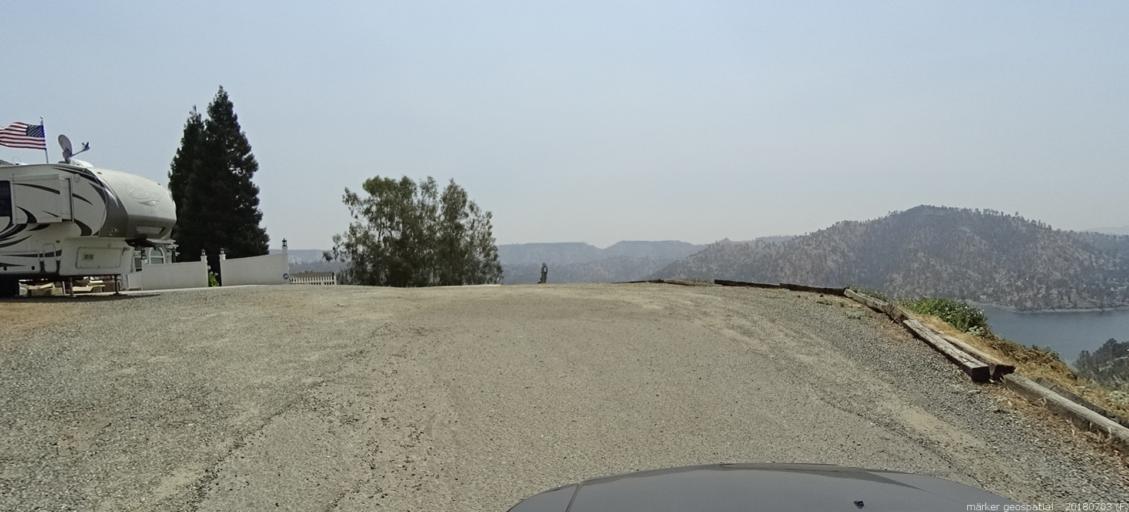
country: US
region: California
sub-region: Fresno County
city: Auberry
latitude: 37.0525
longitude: -119.6531
